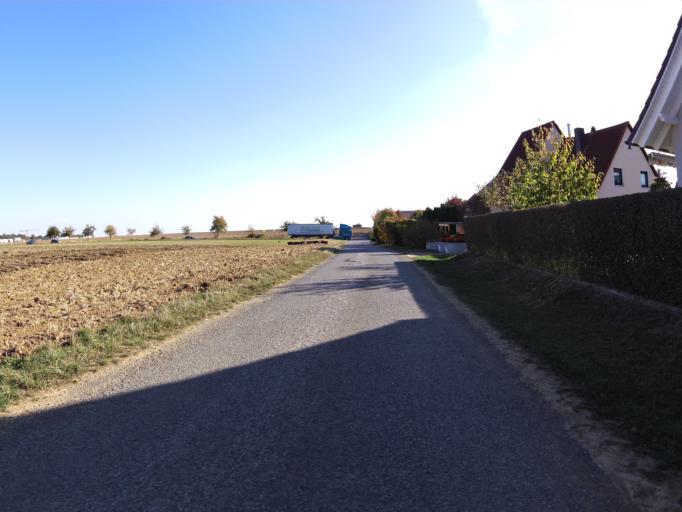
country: DE
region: Bavaria
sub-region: Regierungsbezirk Unterfranken
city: Geroldshausen
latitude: 49.6947
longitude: 9.9342
